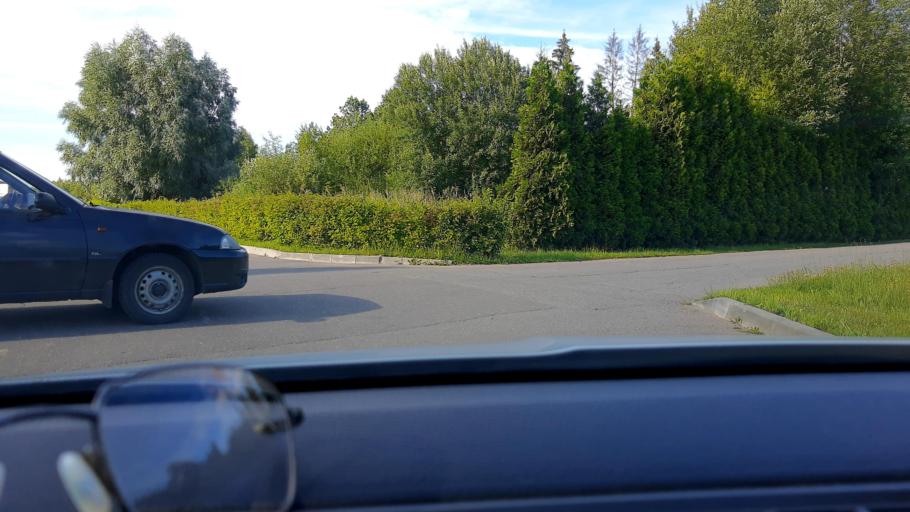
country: RU
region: Moskovskaya
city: Nazar'yevo
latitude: 55.6916
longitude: 37.0401
